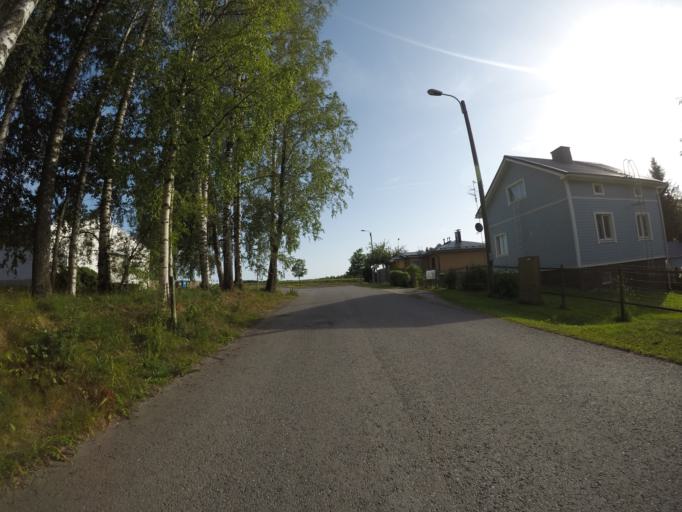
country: FI
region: Haeme
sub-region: Haemeenlinna
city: Haemeenlinna
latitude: 60.9789
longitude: 24.4159
